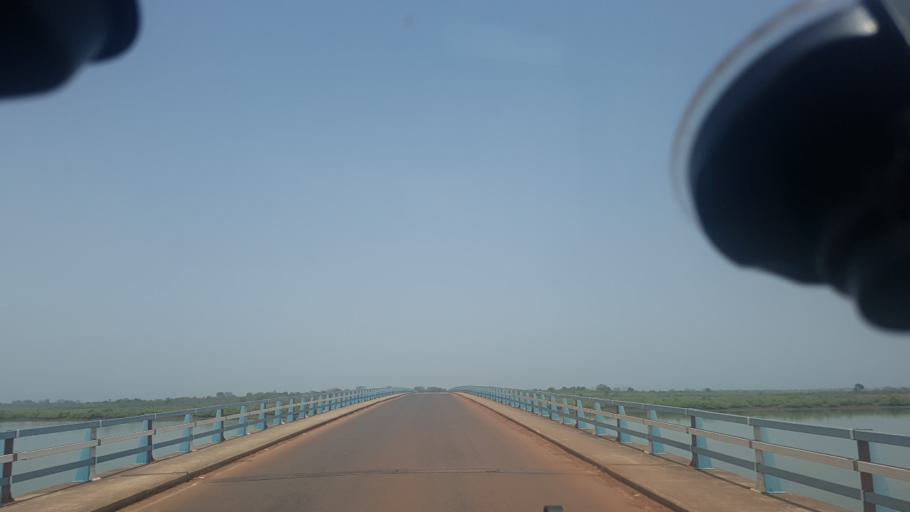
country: GW
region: Bissau
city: Bissau
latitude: 12.0143
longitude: -15.6878
